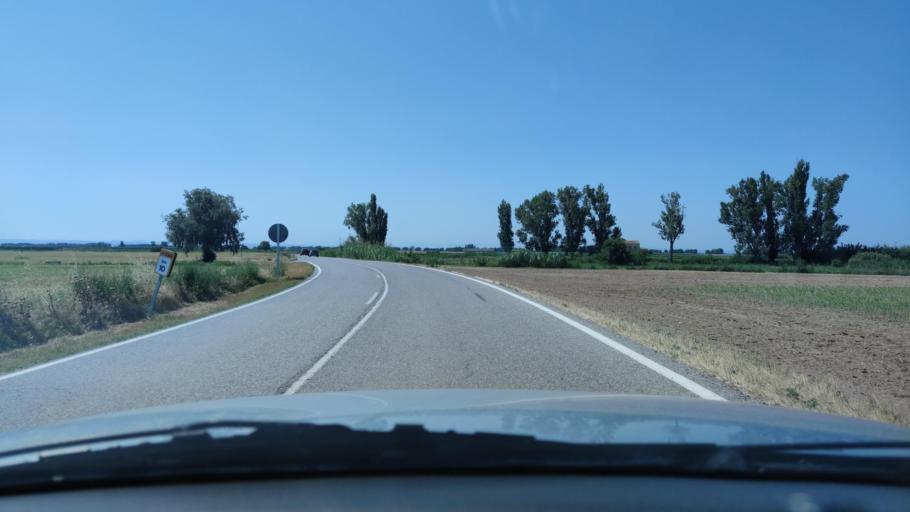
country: ES
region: Catalonia
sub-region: Provincia de Lleida
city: Ivars d'Urgell
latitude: 41.7112
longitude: 0.9822
